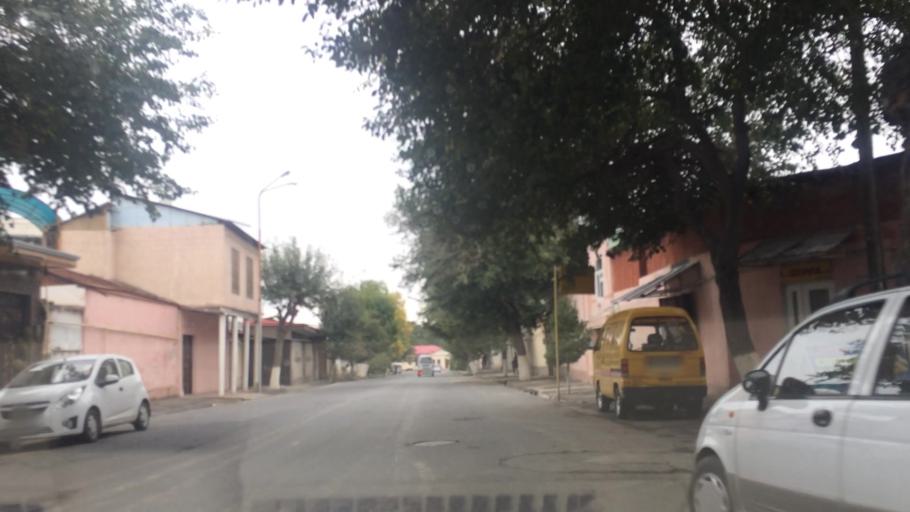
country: UZ
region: Samarqand
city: Samarqand
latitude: 39.6591
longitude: 66.9726
